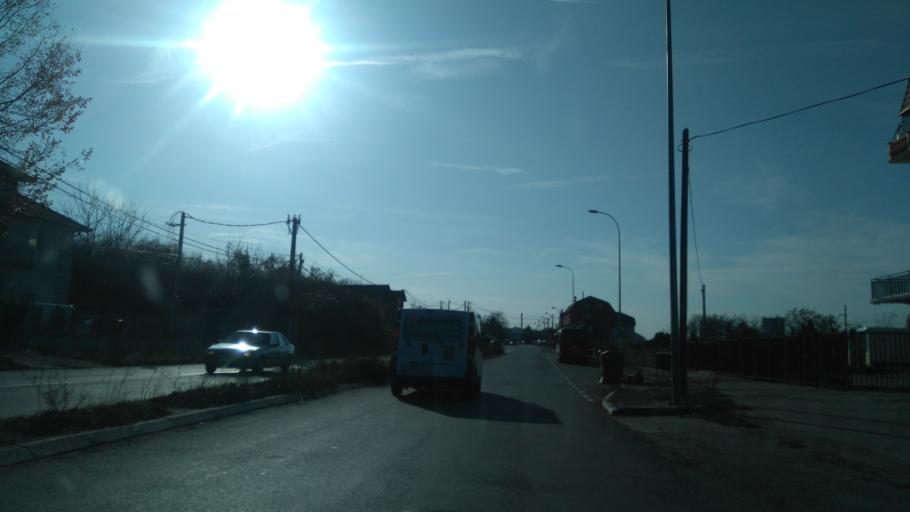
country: RS
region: Central Serbia
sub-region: Belgrade
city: Cukarica
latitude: 44.7413
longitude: 20.3901
